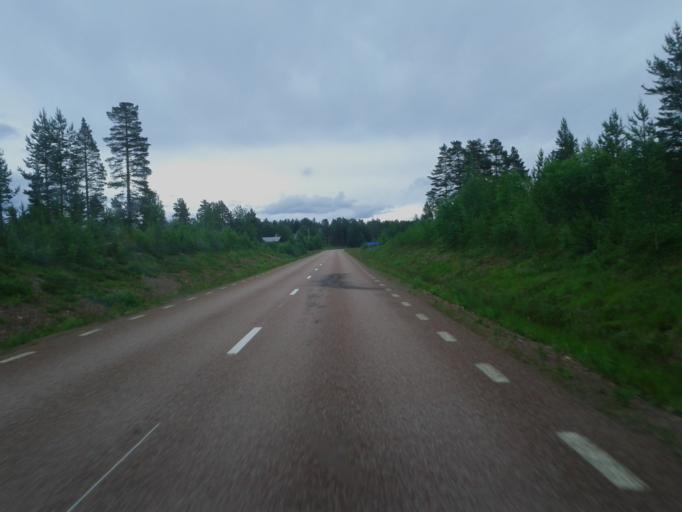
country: SE
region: Dalarna
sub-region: Alvdalens Kommun
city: AElvdalen
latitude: 61.5331
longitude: 13.3521
